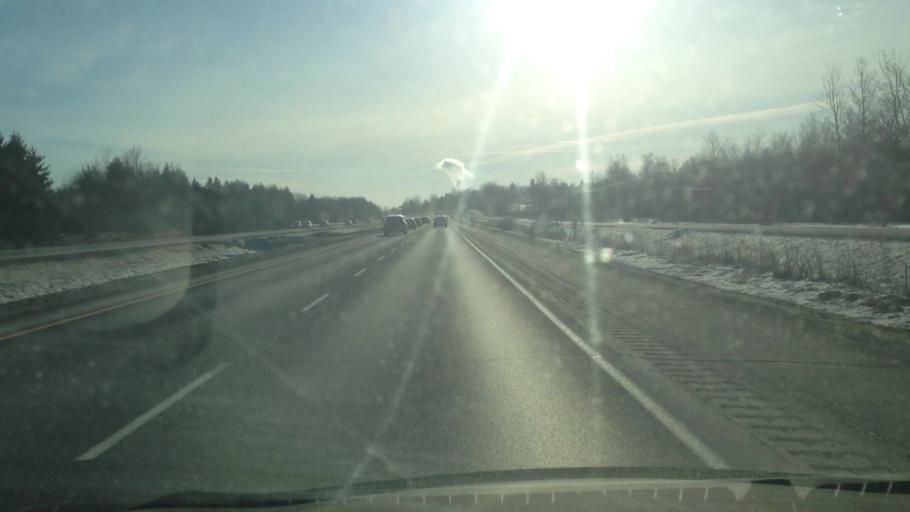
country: CA
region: Quebec
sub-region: Laurentides
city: Prevost
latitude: 45.8199
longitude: -74.0544
